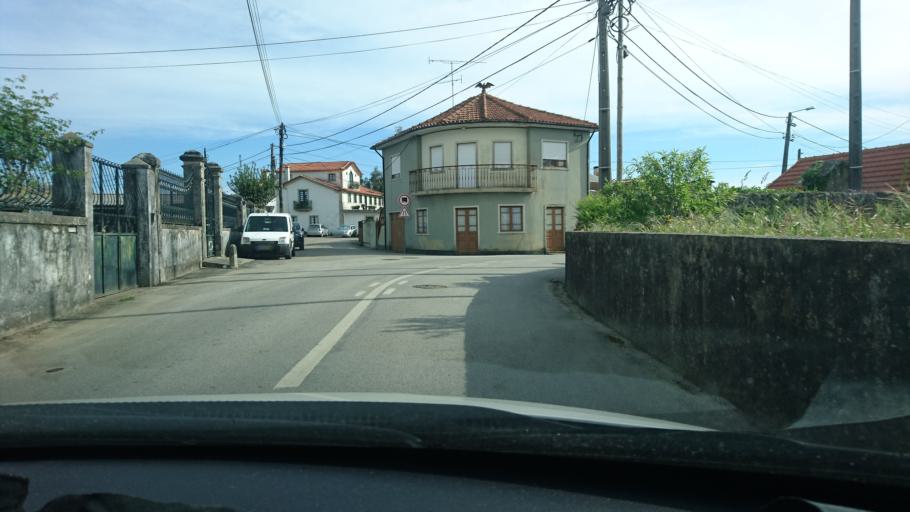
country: PT
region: Aveiro
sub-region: Oliveira de Azemeis
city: Sao Roque
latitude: 40.8792
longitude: -8.4751
